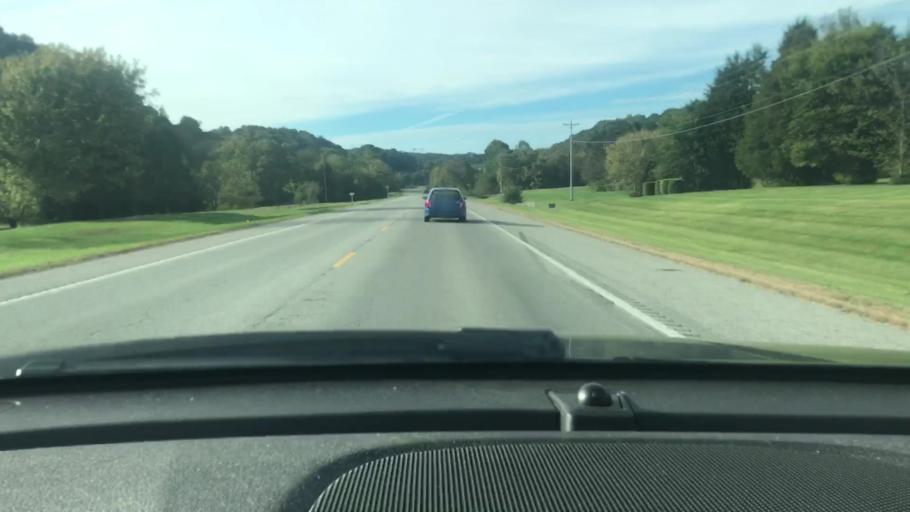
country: US
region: Tennessee
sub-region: Williamson County
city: Franklin
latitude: 35.9546
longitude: -86.9562
